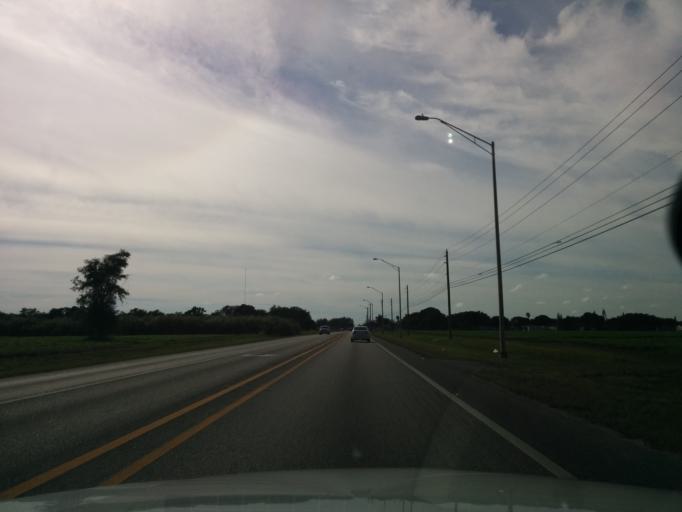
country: US
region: Florida
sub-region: Miami-Dade County
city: Richmond West
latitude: 25.5866
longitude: -80.4784
